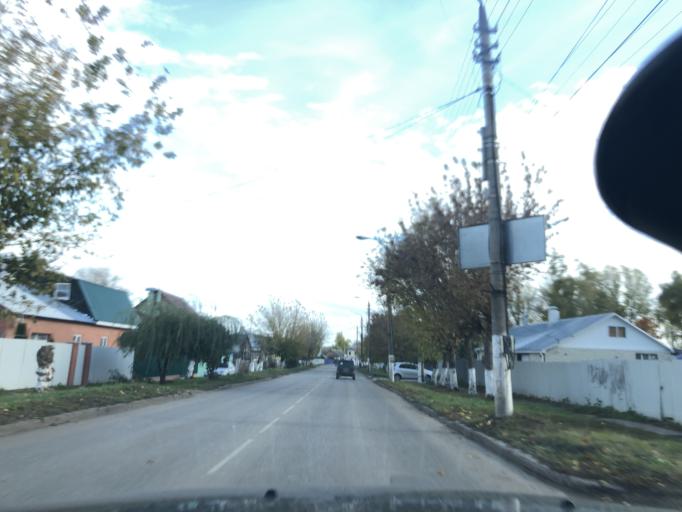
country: RU
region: Tula
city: Kireyevsk
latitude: 53.9326
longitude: 37.9250
